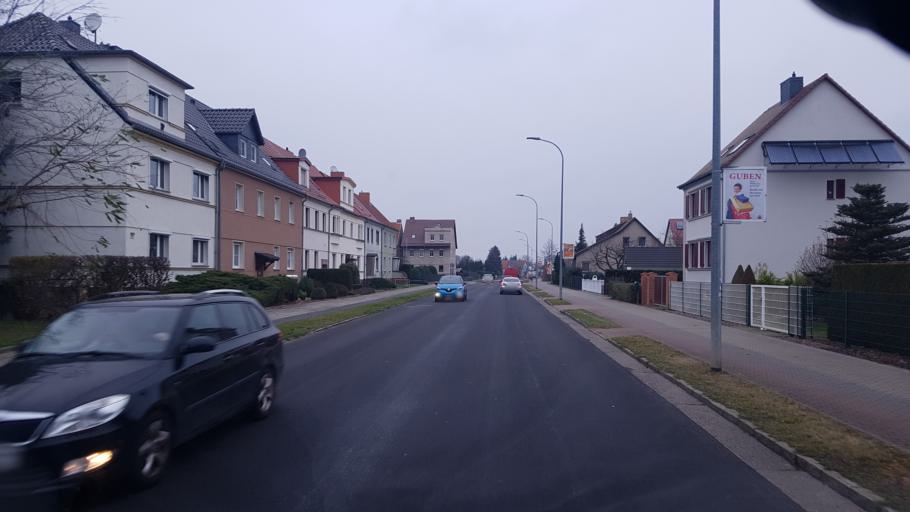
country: DE
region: Brandenburg
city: Guben
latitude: 51.9490
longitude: 14.7031
